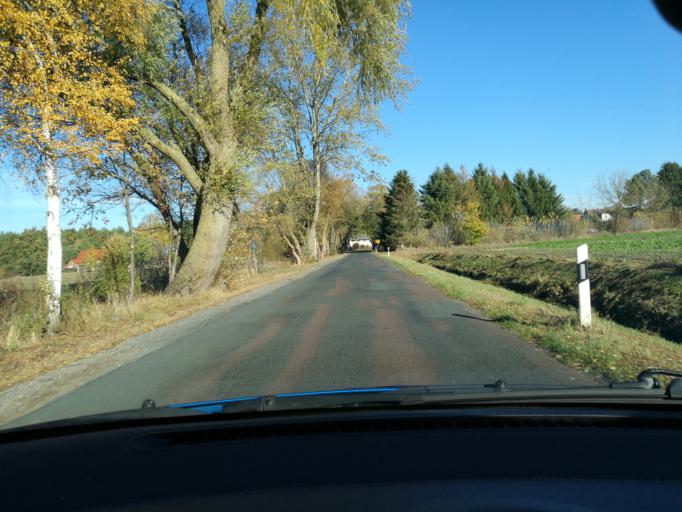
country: DE
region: Mecklenburg-Vorpommern
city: Neu Kaliss
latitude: 53.1565
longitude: 11.3162
